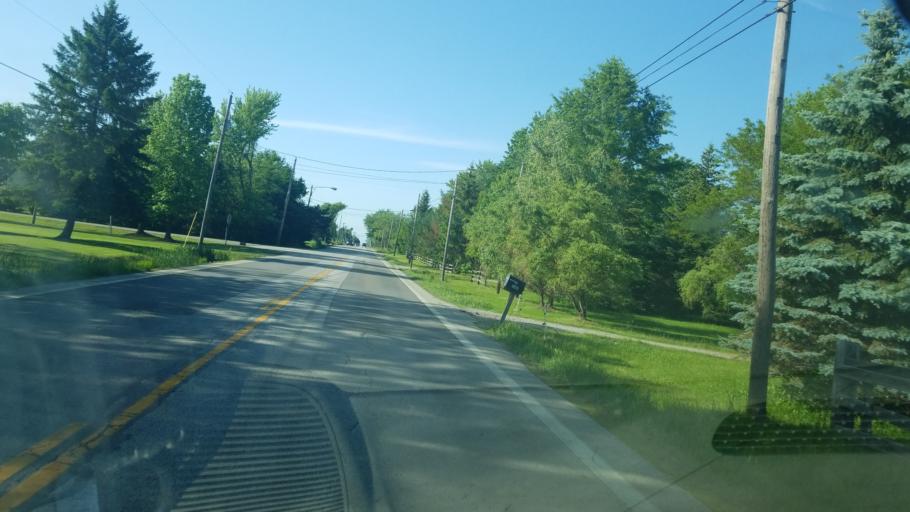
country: US
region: Ohio
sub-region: Medina County
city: Seville
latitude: 41.0727
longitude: -81.8643
